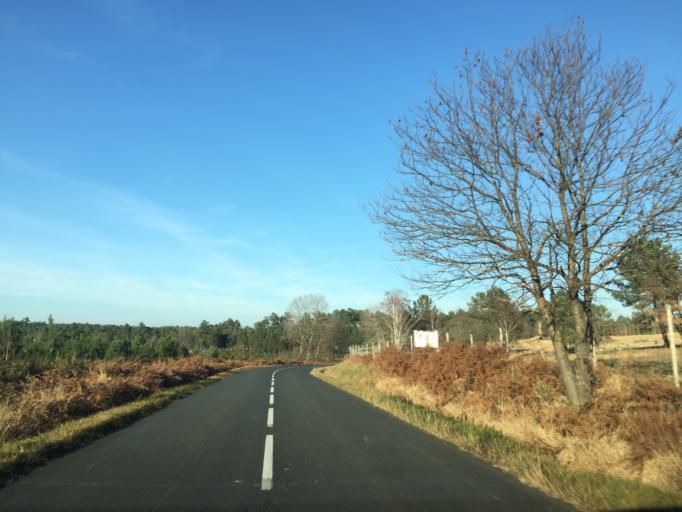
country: FR
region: Aquitaine
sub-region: Departement de la Dordogne
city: Neuvic
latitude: 45.1488
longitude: 0.4273
